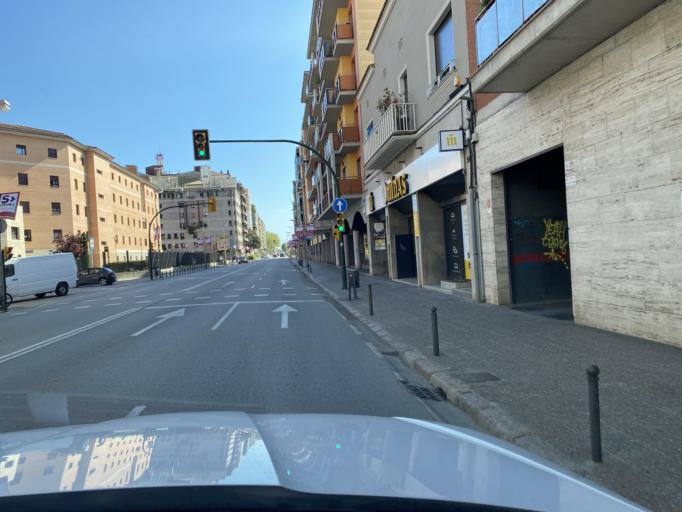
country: ES
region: Catalonia
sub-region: Provincia de Girona
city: Girona
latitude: 41.9785
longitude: 2.8178
